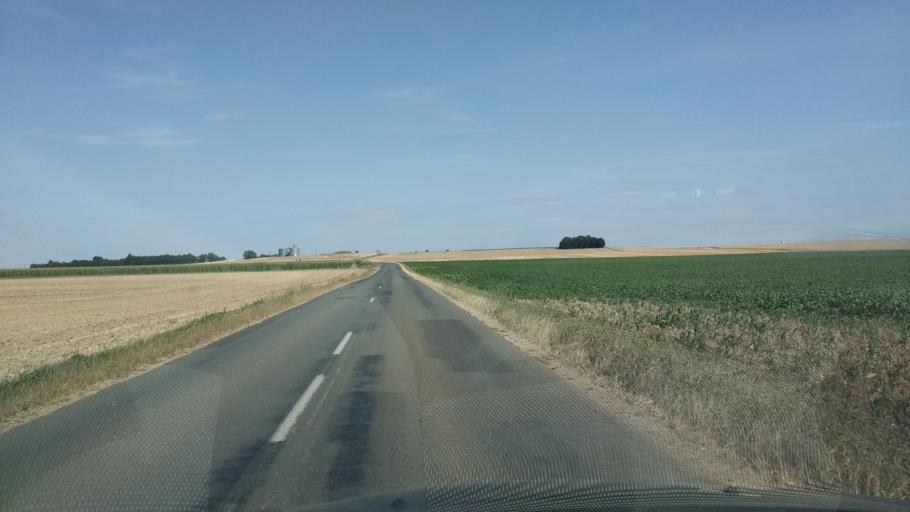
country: FR
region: Poitou-Charentes
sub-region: Departement de la Vienne
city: Vouille
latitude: 46.6857
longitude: 0.1555
